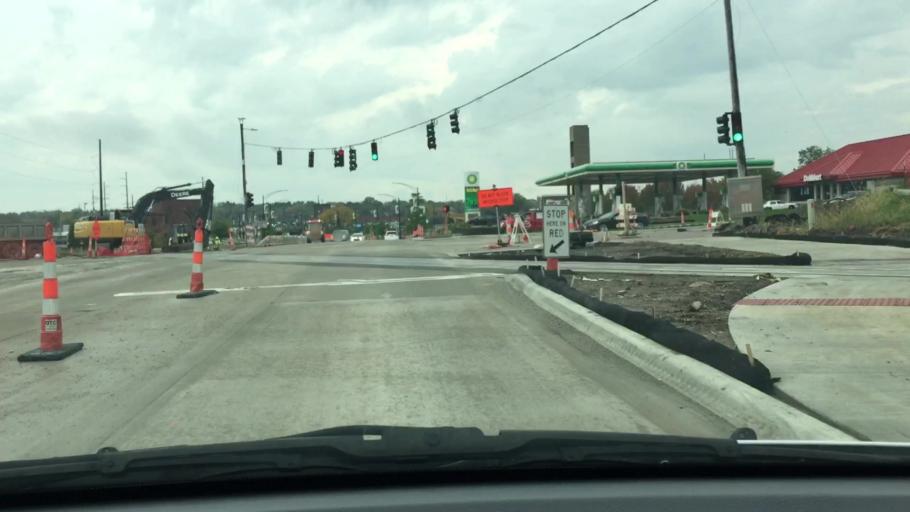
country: US
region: Iowa
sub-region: Johnson County
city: Coralville
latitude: 41.6770
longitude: -91.5661
